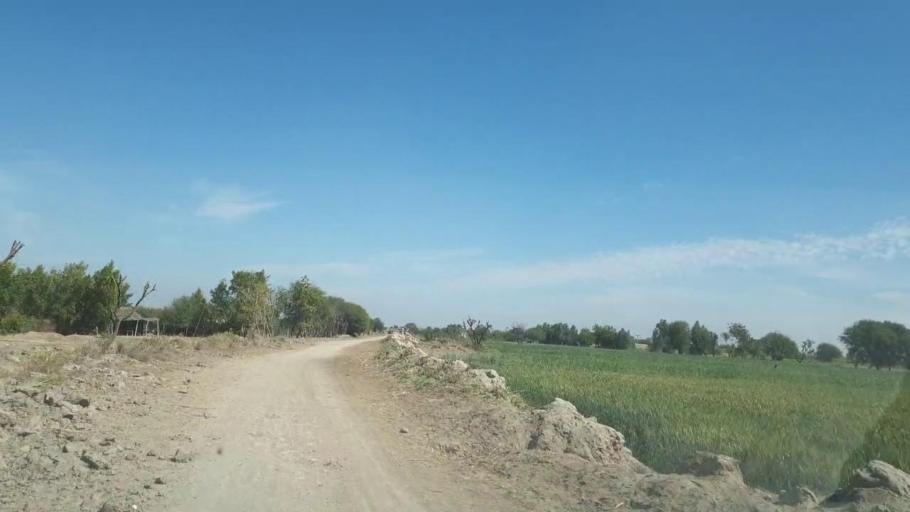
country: PK
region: Sindh
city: Pithoro
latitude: 25.6068
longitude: 69.2842
